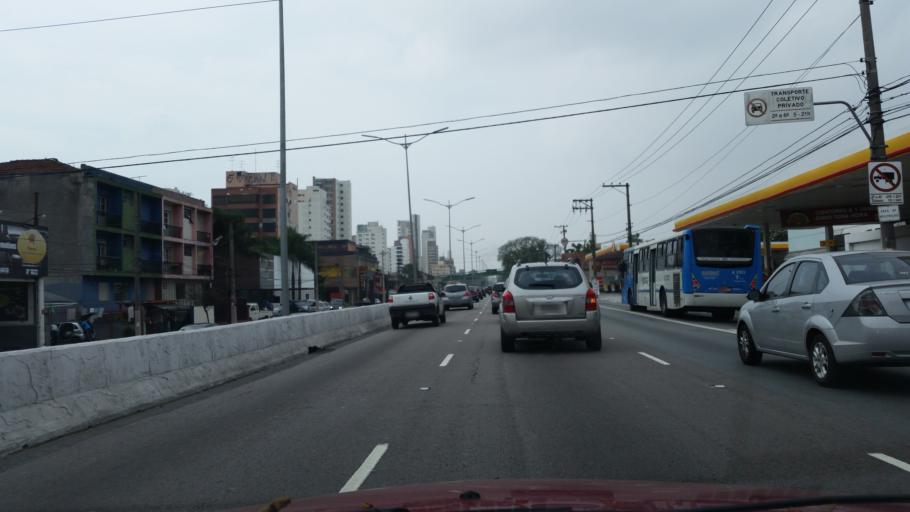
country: BR
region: Sao Paulo
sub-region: Sao Paulo
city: Sao Paulo
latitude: -23.6151
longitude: -46.6595
